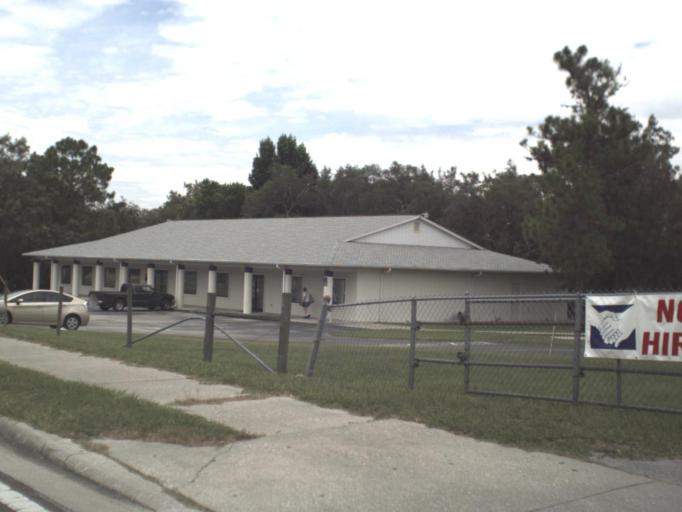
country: US
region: Florida
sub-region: Citrus County
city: Lecanto
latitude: 28.8778
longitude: -82.5231
